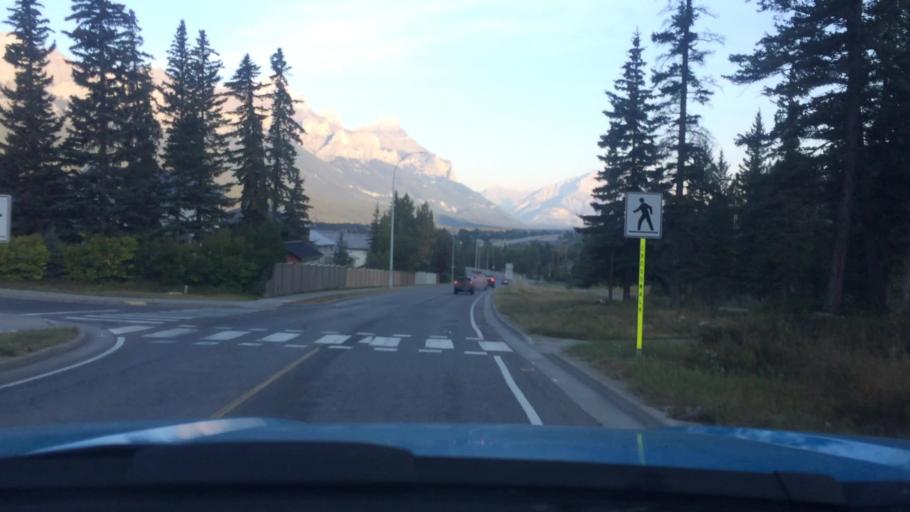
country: CA
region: Alberta
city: Canmore
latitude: 51.0885
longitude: -115.3364
